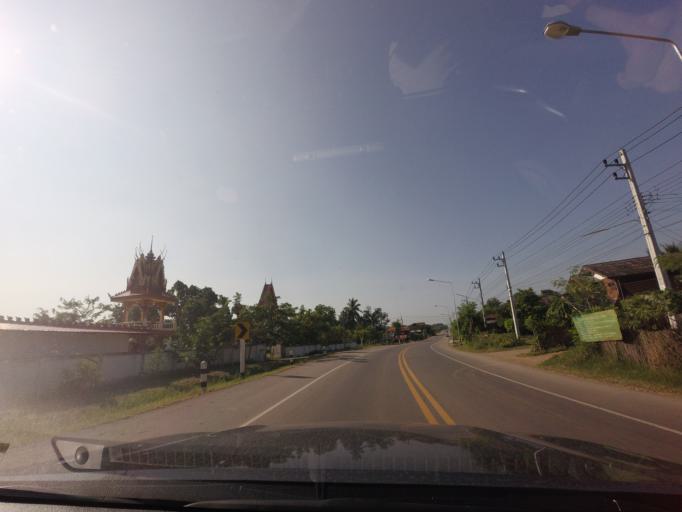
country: TH
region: Phetchabun
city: Lom Sak
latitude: 16.8105
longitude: 101.1825
